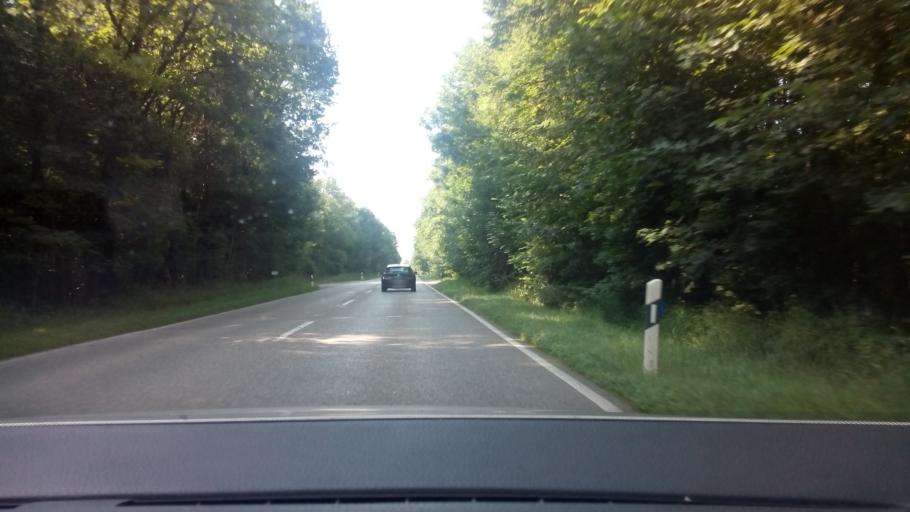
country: DE
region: Bavaria
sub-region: Upper Bavaria
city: Oberschleissheim
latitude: 48.2382
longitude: 11.5827
